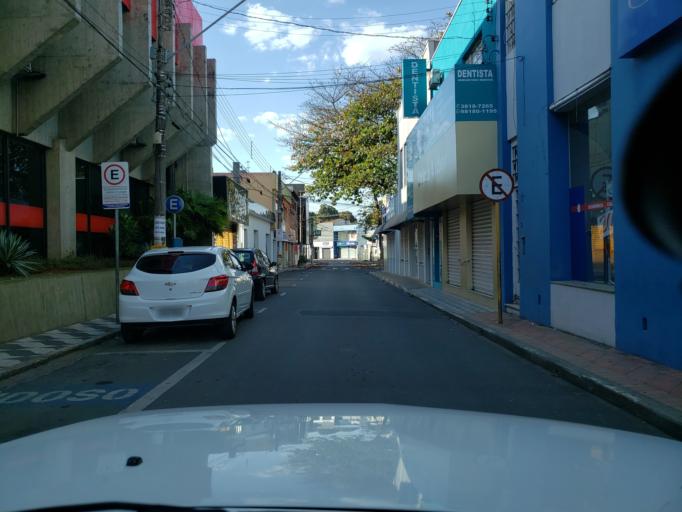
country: BR
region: Sao Paulo
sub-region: Moji-Guacu
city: Mogi-Gaucu
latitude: -22.3712
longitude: -46.9427
